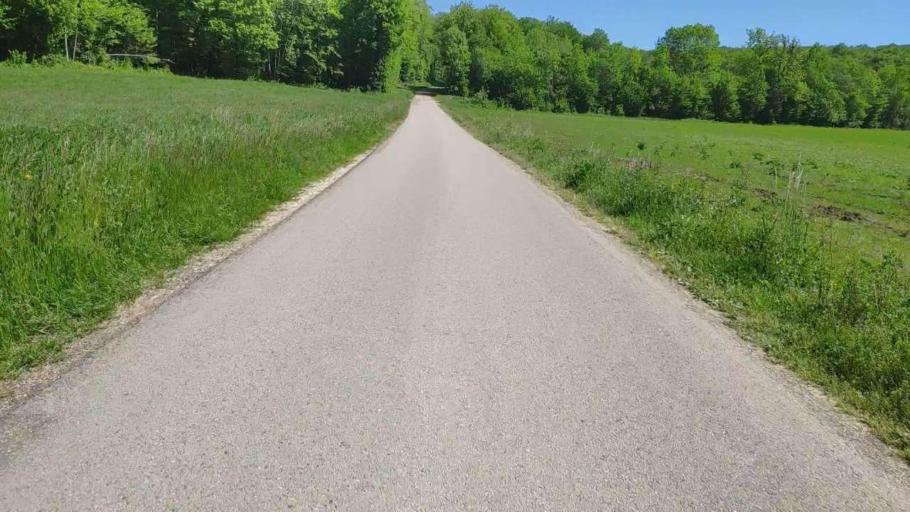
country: FR
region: Franche-Comte
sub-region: Departement du Jura
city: Poligny
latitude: 46.7416
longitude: 5.7721
